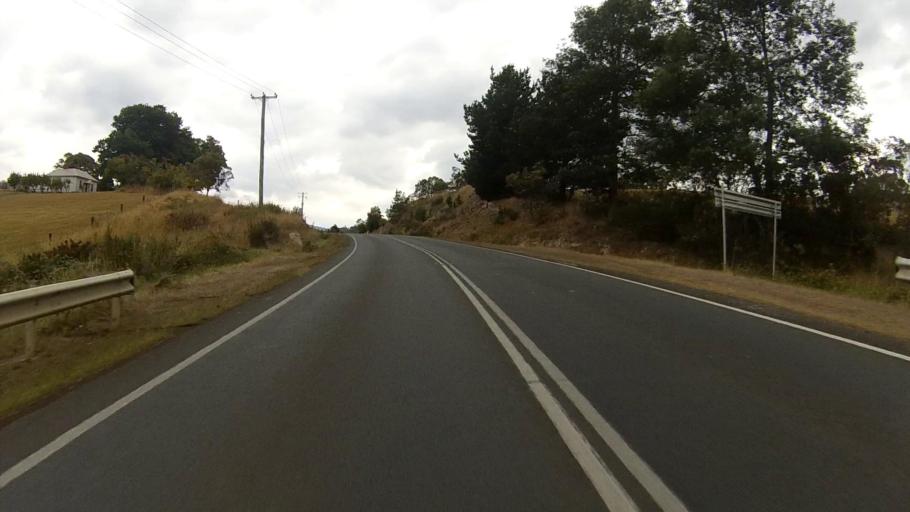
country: AU
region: Tasmania
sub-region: Huon Valley
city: Franklin
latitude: -43.1131
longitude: 147.0365
